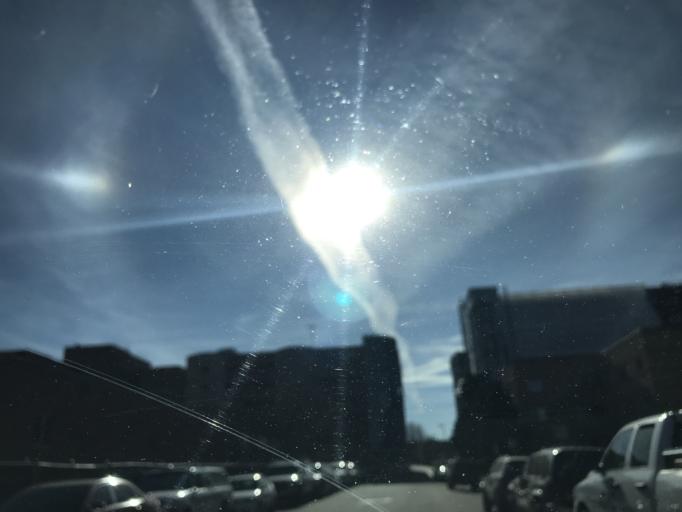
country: US
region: Colorado
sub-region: Arapahoe County
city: Glendale
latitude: 39.7337
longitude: -104.9373
